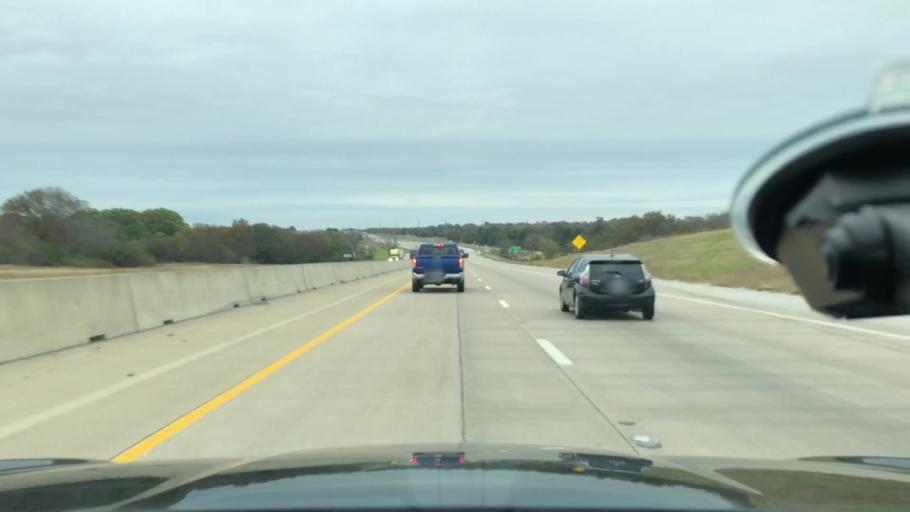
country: US
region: Texas
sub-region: Ellis County
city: Waxahachie
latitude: 32.3423
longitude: -96.8557
